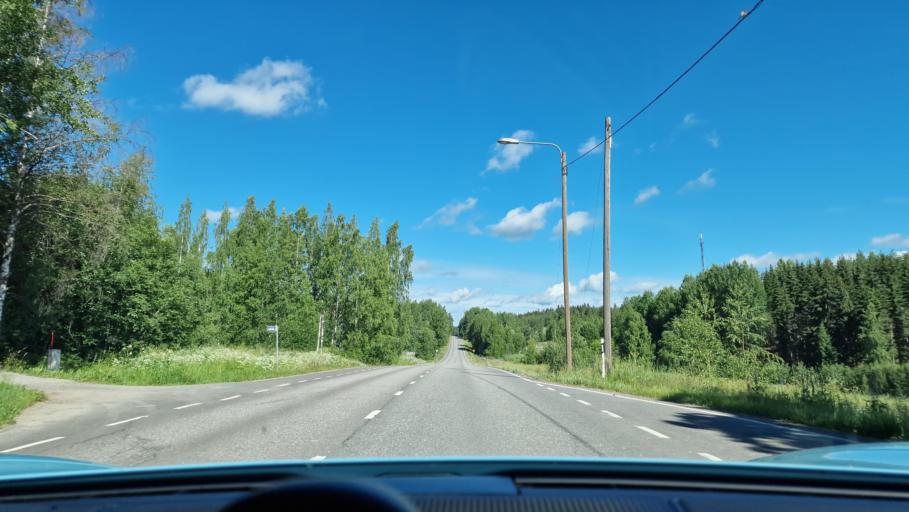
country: FI
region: Pirkanmaa
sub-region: Tampere
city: Orivesi
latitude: 61.6100
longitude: 24.3087
